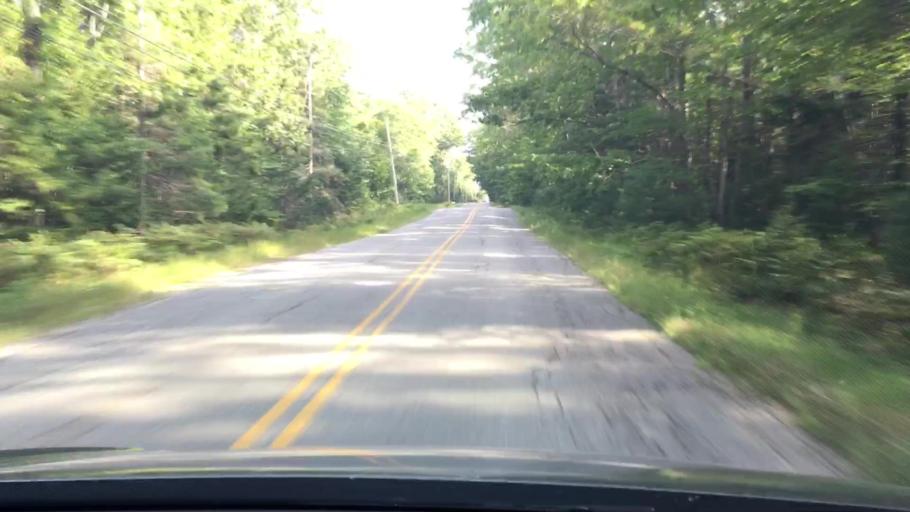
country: US
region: Maine
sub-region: Hancock County
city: Bucksport
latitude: 44.5345
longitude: -68.7935
